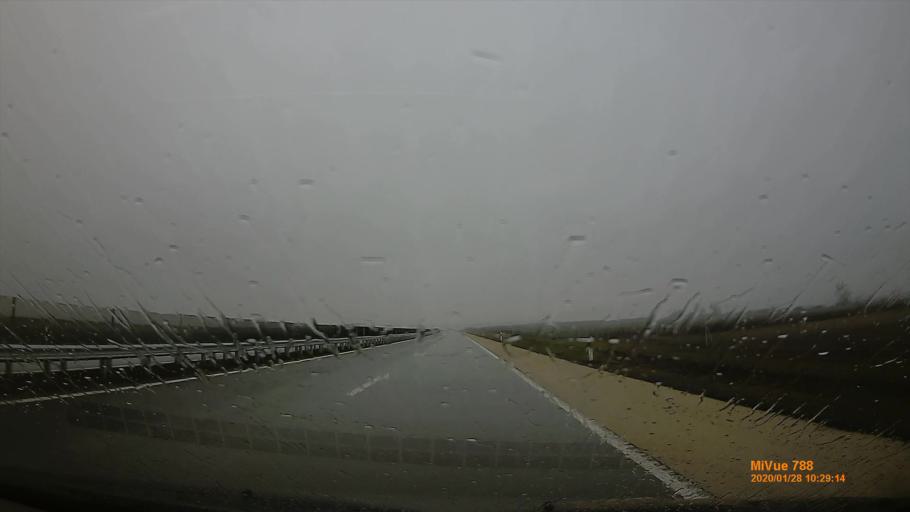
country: HU
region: Pest
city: Pilis
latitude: 47.3229
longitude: 19.5363
